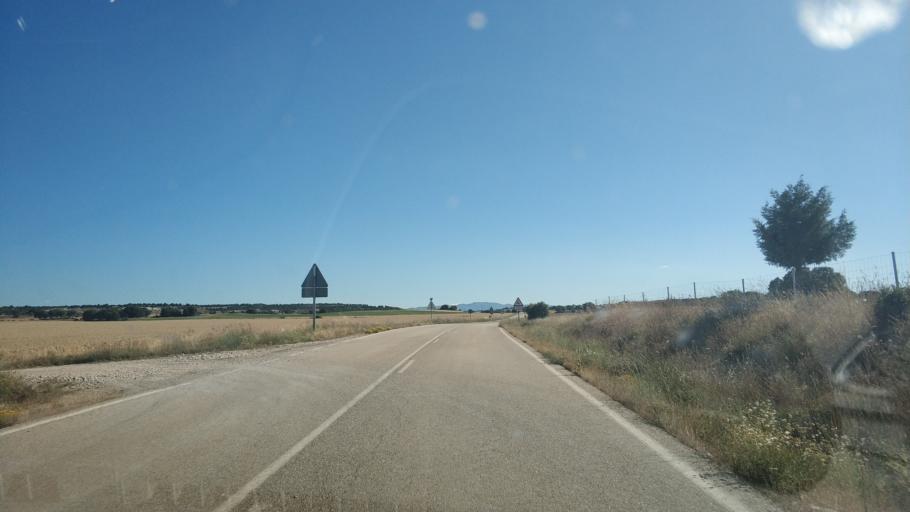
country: ES
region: Castille and Leon
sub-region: Provincia de Soria
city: San Esteban de Gormaz
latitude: 41.4973
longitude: -3.2004
